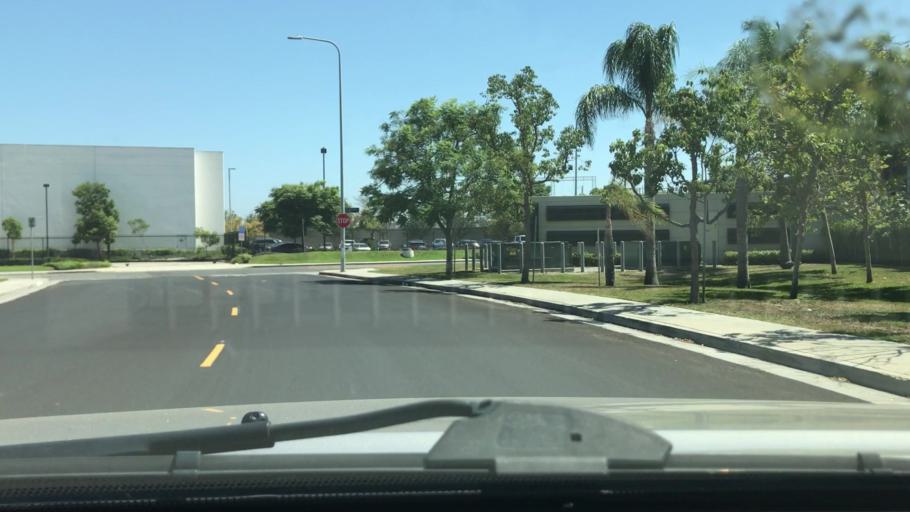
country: US
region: California
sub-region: Los Angeles County
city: Carson
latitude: 33.8505
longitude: -118.3035
